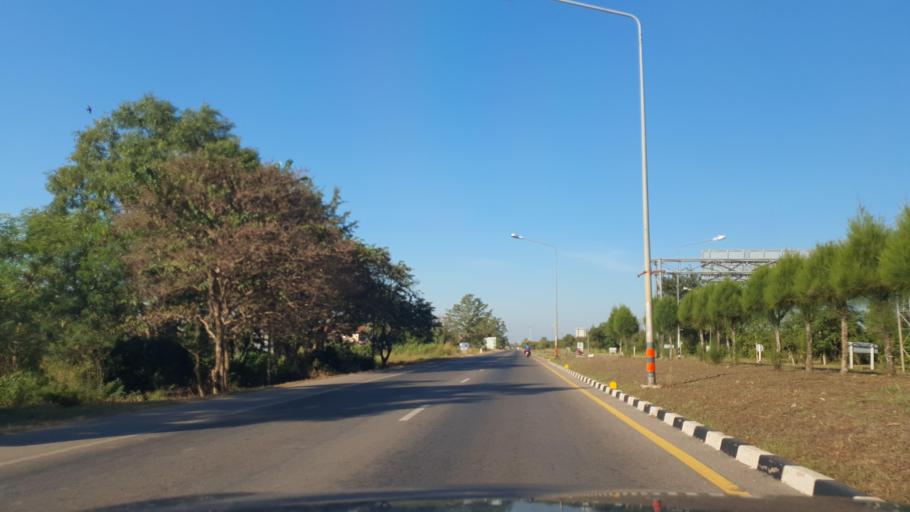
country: TH
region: Sukhothai
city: Sukhothai
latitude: 17.0729
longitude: 99.8292
